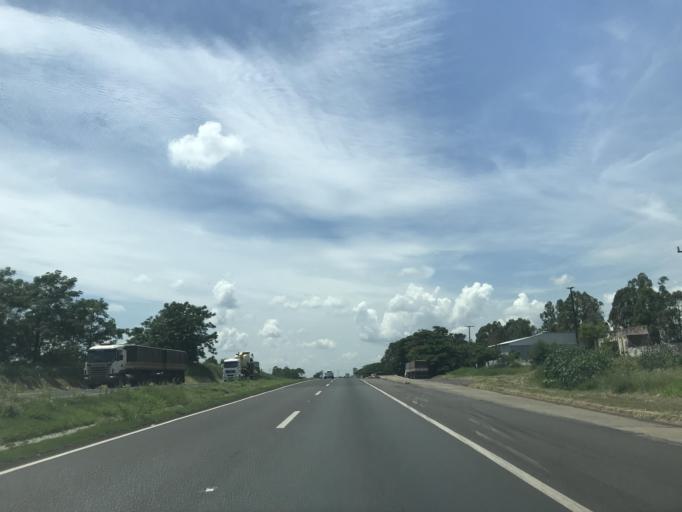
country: BR
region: Parana
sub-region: Alto Parana
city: Alto Parana
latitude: -23.1759
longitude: -52.2321
